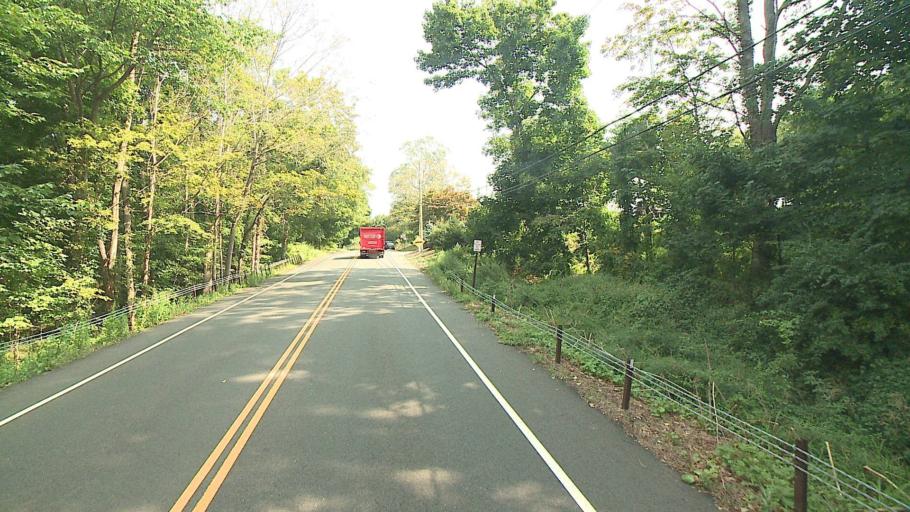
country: US
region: Connecticut
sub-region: Fairfield County
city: Georgetown
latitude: 41.3038
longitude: -73.3830
